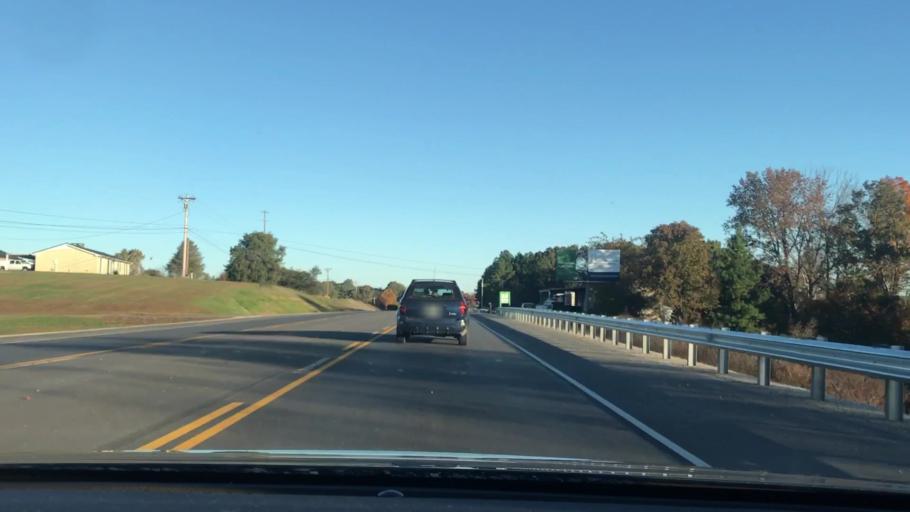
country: US
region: Kentucky
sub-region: Simpson County
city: Franklin
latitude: 36.6822
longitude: -86.5668
